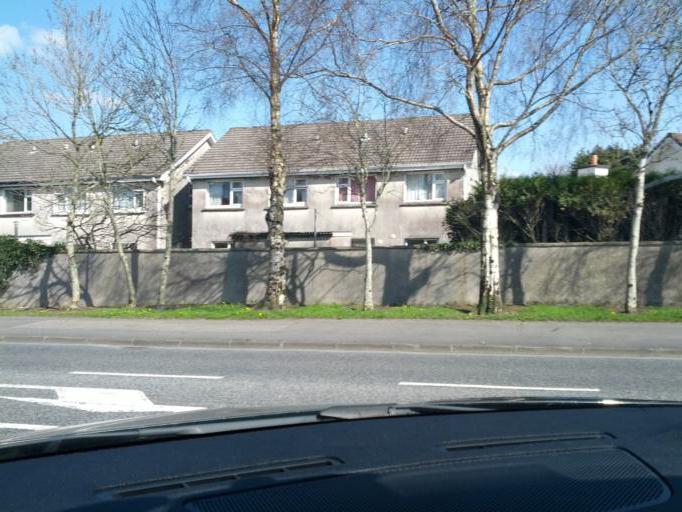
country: IE
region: Connaught
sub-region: County Galway
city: Gaillimh
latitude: 53.2874
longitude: -9.0751
